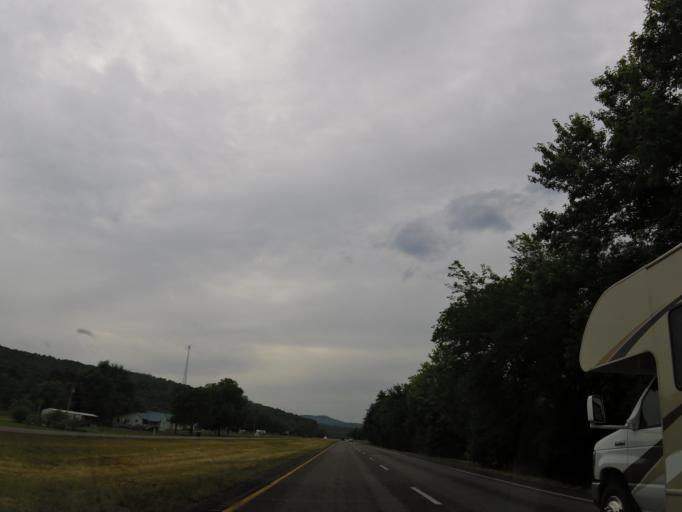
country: US
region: Alabama
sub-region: Madison County
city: New Hope
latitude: 34.6673
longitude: -86.3289
